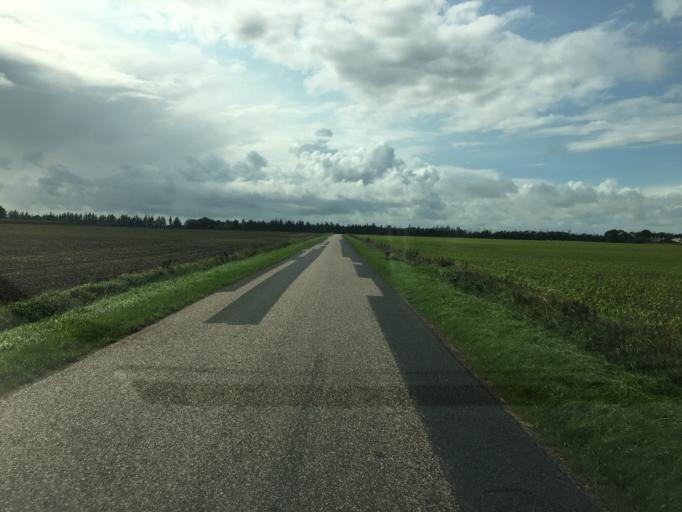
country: DK
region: South Denmark
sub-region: Tonder Kommune
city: Tonder
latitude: 54.9787
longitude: 8.8482
